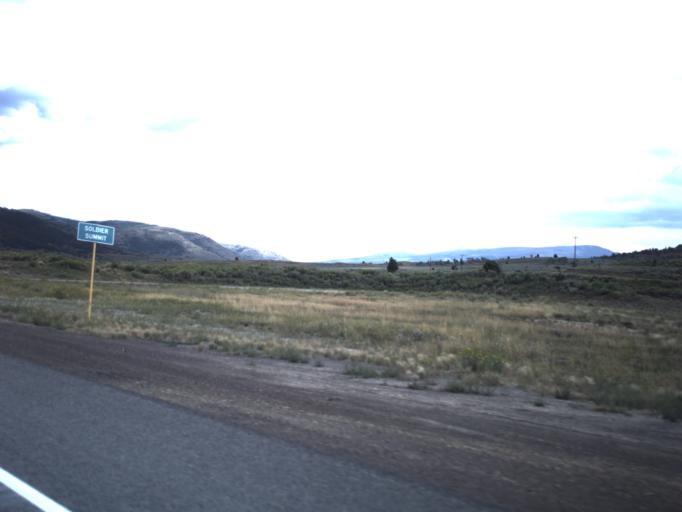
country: US
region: Utah
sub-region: Carbon County
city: Helper
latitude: 39.9285
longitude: -111.0838
